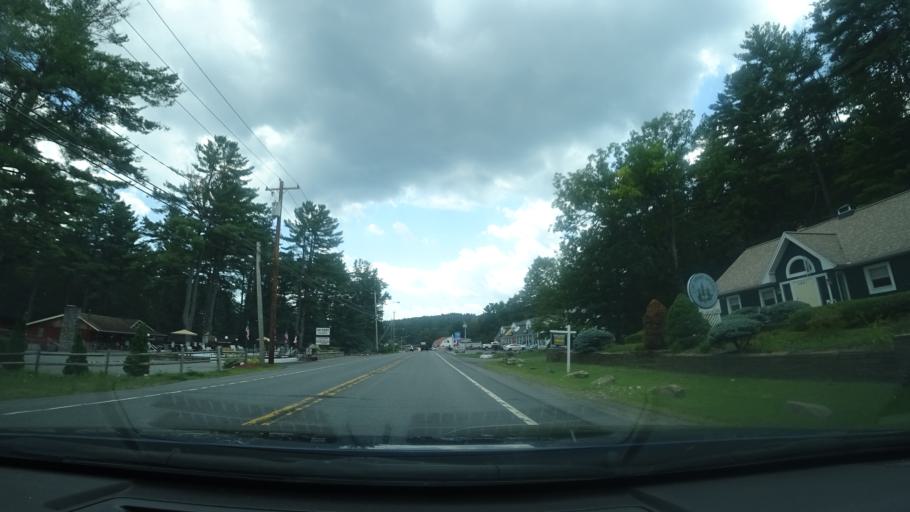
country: US
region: New York
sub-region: Warren County
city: Glens Falls North
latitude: 43.3918
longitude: -73.7043
